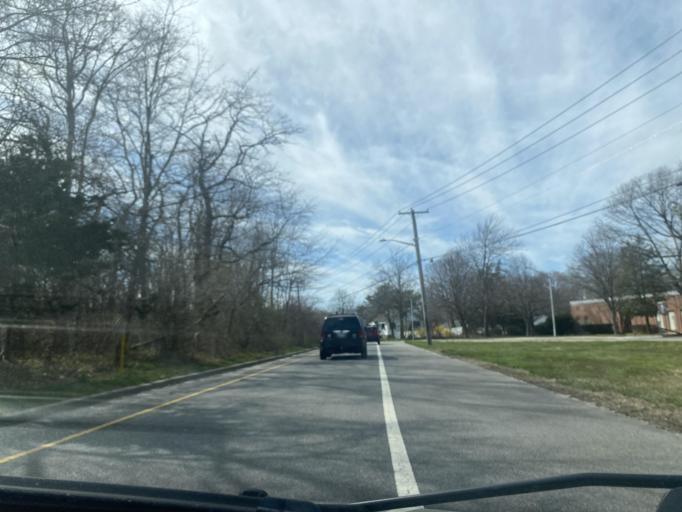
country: US
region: New York
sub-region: Suffolk County
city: Rocky Point
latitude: 40.9476
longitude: -72.9072
